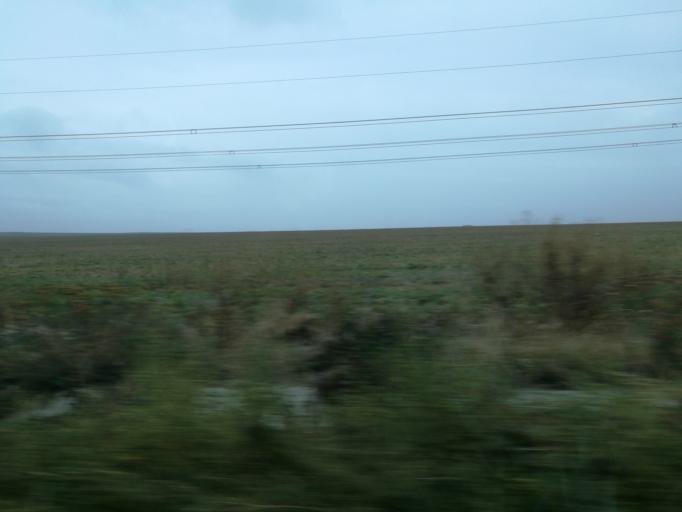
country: RO
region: Constanta
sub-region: Comuna Mihail Kogalniceanu
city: Piatra
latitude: 44.4607
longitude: 28.5578
